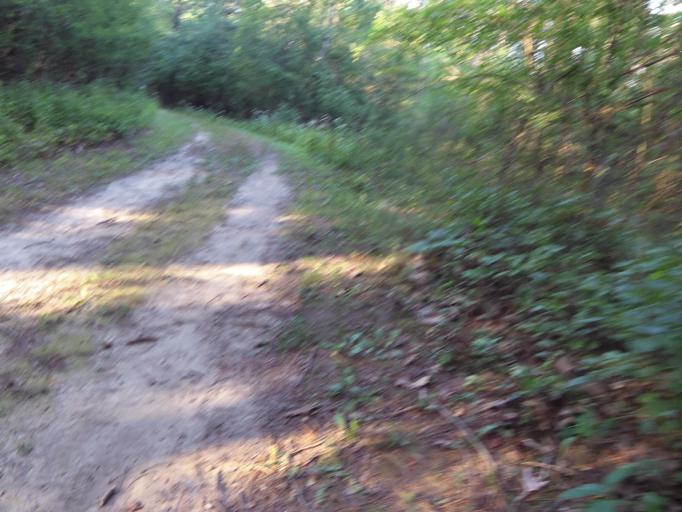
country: US
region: Minnesota
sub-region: Washington County
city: Afton
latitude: 44.8462
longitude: -92.7734
